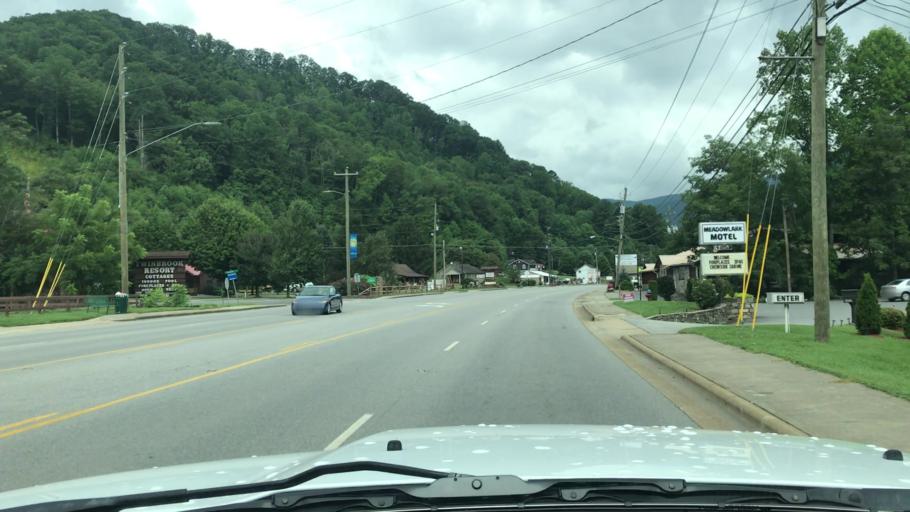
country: US
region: North Carolina
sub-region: Haywood County
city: Maggie Valley
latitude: 35.5122
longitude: -83.0767
